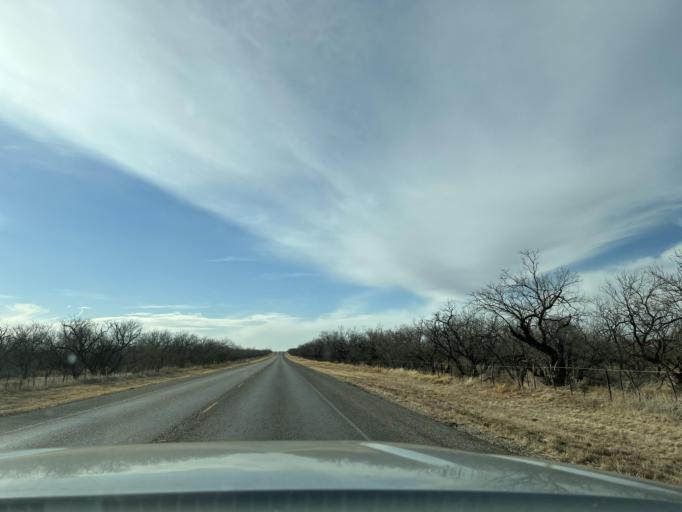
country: US
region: Texas
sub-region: Fisher County
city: Rotan
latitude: 32.7398
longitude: -100.5168
